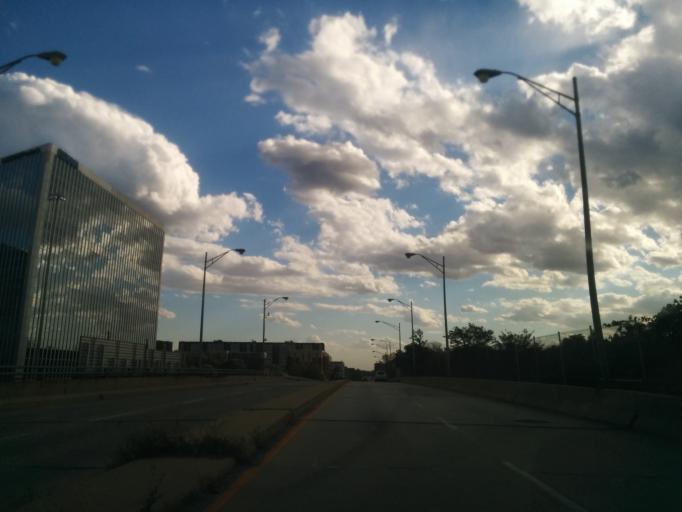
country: US
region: Illinois
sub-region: Cook County
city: Park Ridge
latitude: 41.9845
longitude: -87.8465
